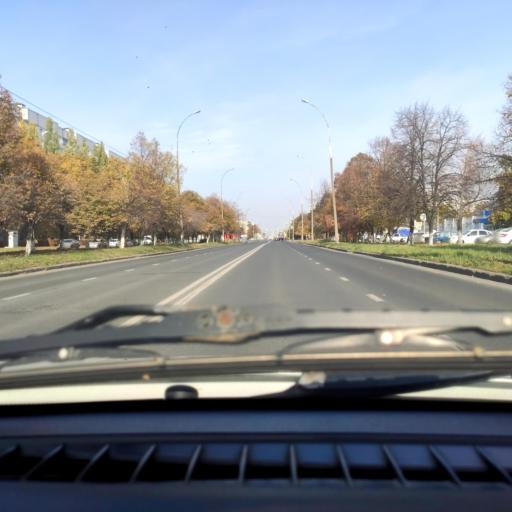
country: RU
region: Samara
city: Tol'yatti
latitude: 53.5313
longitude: 49.3131
